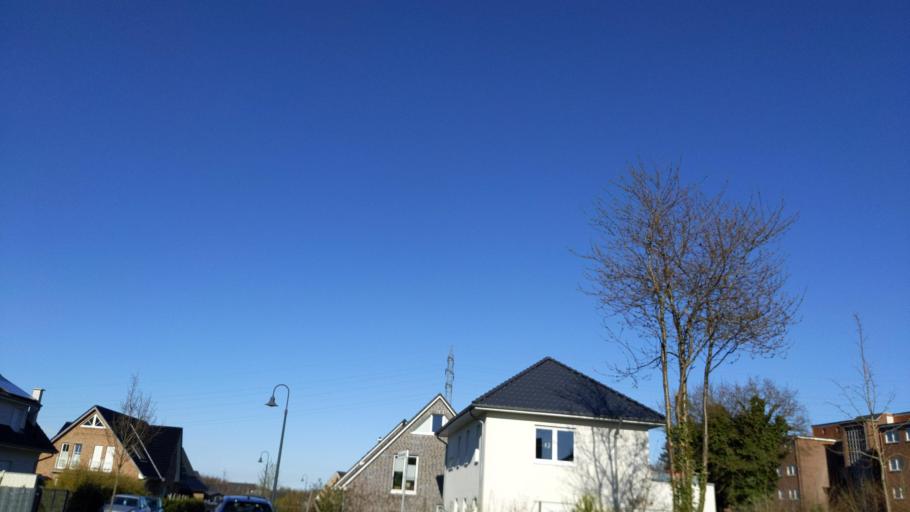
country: DE
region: Schleswig-Holstein
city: Scharbeutz
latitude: 54.0227
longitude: 10.7357
